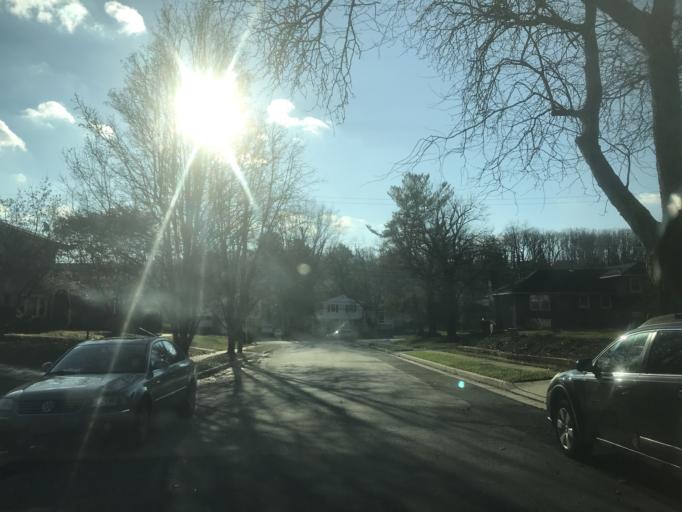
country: US
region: Maryland
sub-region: Baltimore County
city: Towson
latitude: 39.4033
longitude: -76.5848
